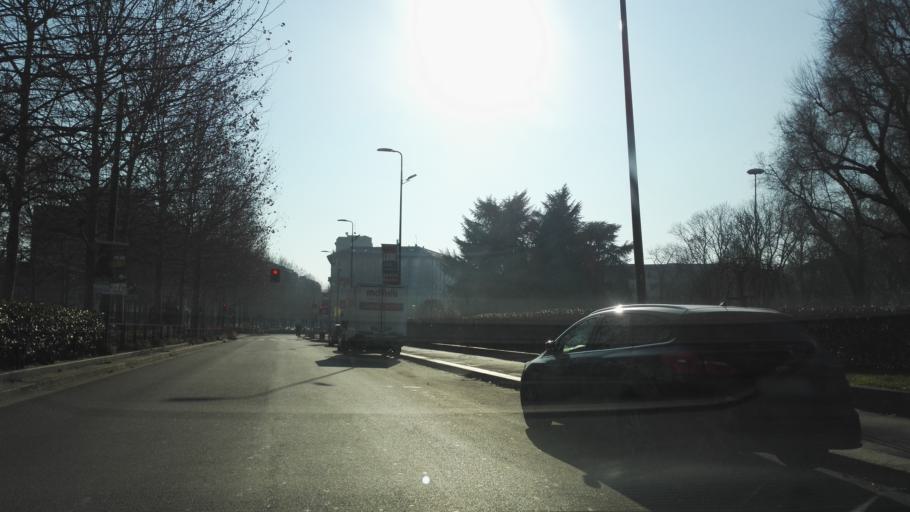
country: IT
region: Lombardy
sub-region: Citta metropolitana di Milano
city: Milano
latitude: 45.4603
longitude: 9.2173
